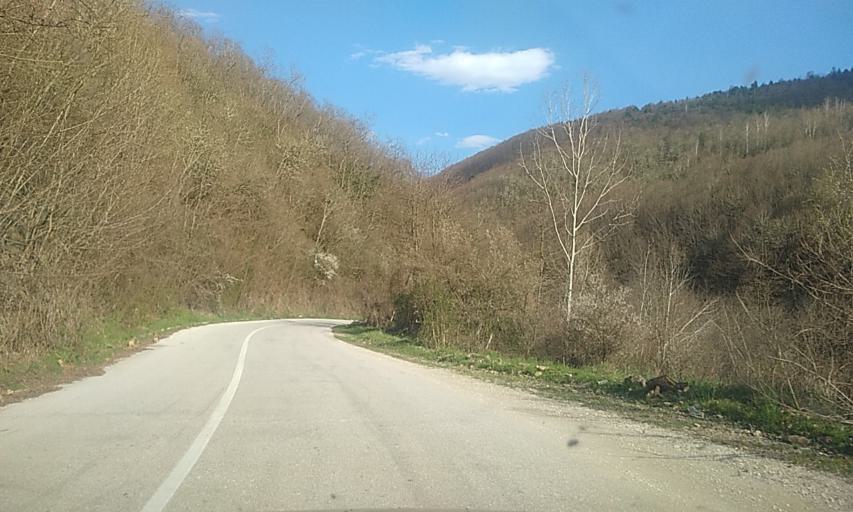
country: RS
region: Central Serbia
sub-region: Pcinjski Okrug
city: Bosilegrad
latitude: 42.4176
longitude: 22.5155
